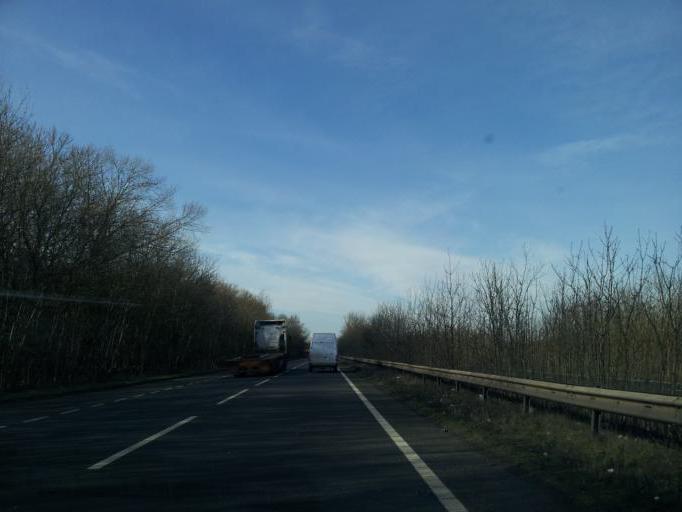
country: GB
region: England
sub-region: District of Rutland
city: Tickencote
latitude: 52.6923
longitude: -0.5638
